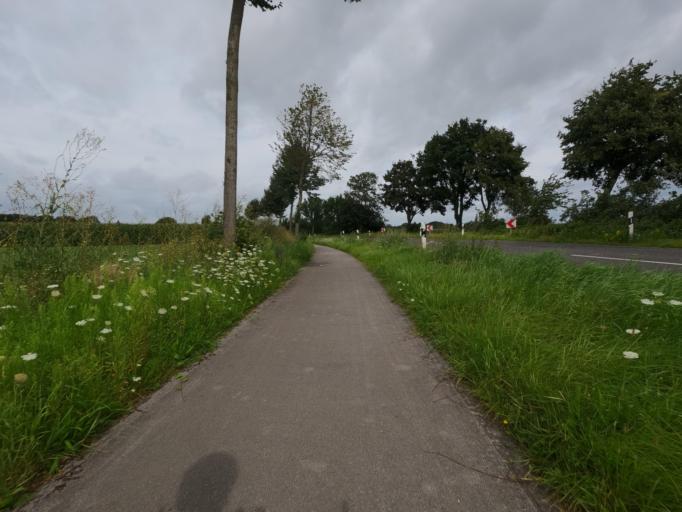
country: DE
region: North Rhine-Westphalia
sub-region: Regierungsbezirk Koln
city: Heinsberg
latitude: 51.0324
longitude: 6.1542
